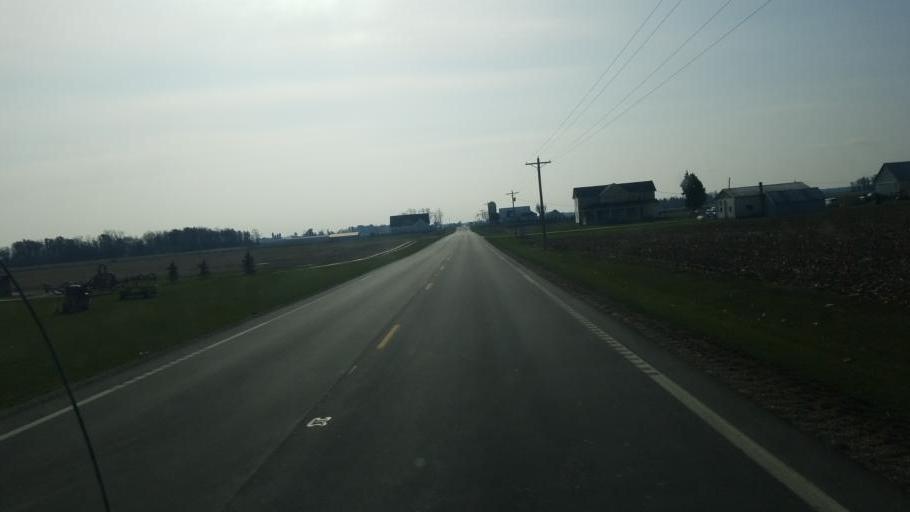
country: US
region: Ohio
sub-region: Mercer County
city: Fort Recovery
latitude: 40.5012
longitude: -84.7844
